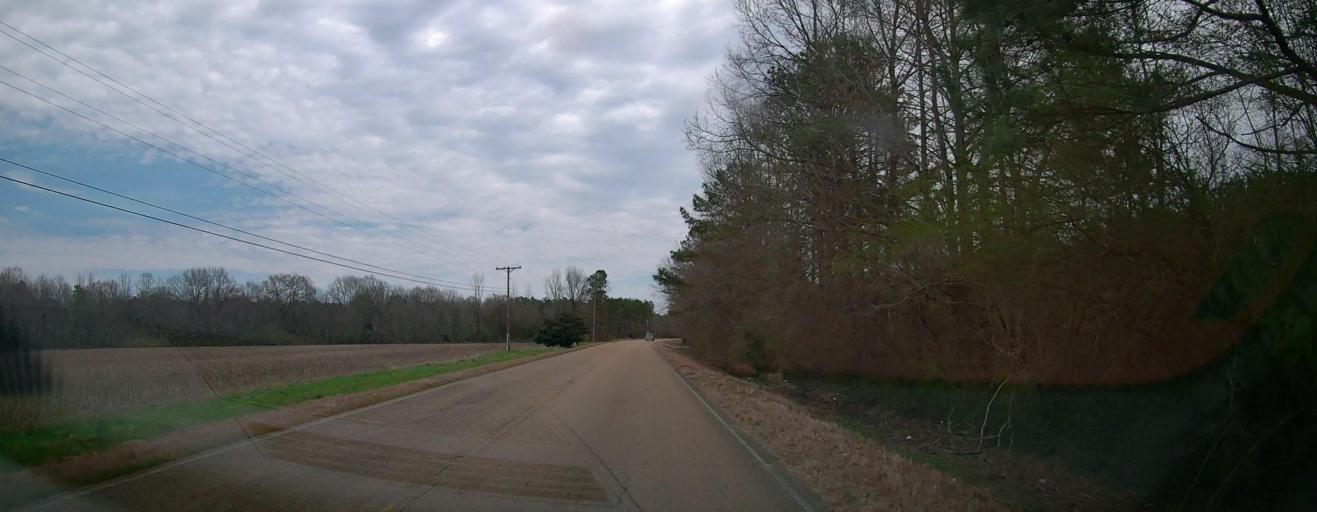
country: US
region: Mississippi
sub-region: Itawamba County
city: Fulton
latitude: 34.2303
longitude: -88.2422
